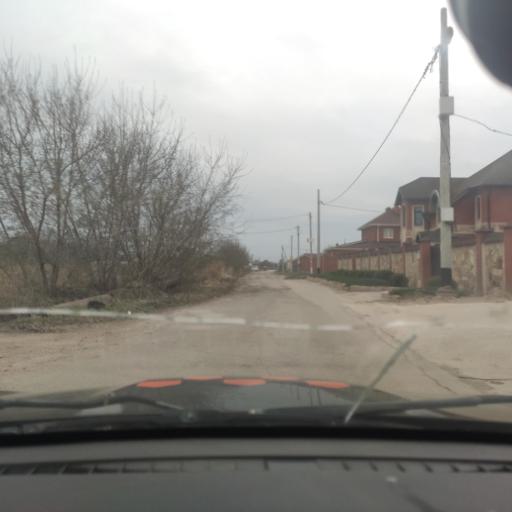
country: RU
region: Samara
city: Podstepki
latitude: 53.5104
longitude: 49.1105
